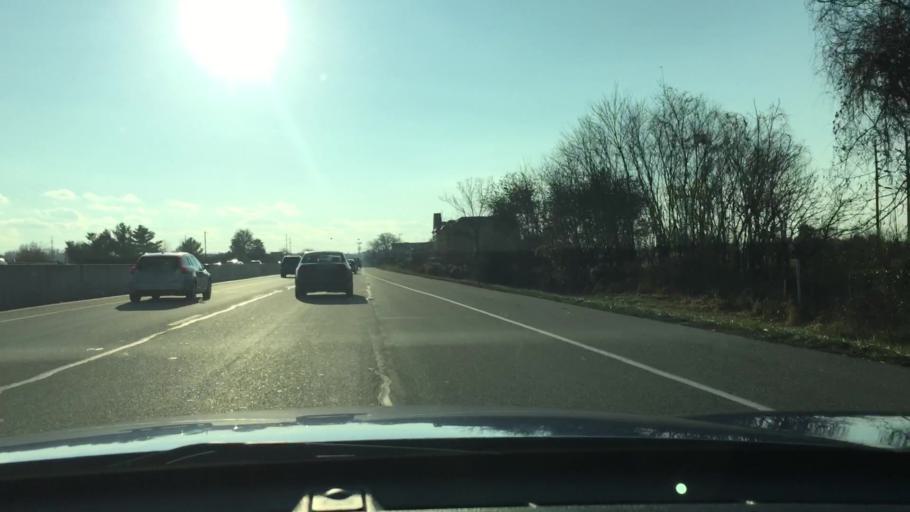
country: US
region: Pennsylvania
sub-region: Cumberland County
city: Shiremanstown
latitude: 40.2057
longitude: -76.9635
